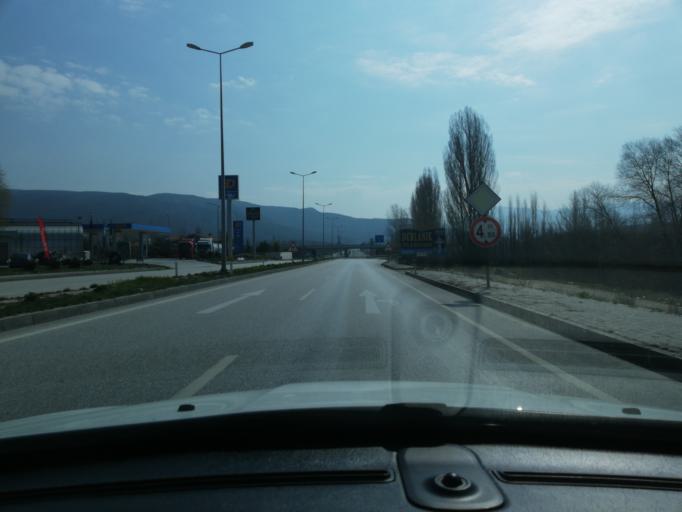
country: TR
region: Cankiri
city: Ilgaz
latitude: 40.9059
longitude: 33.6467
